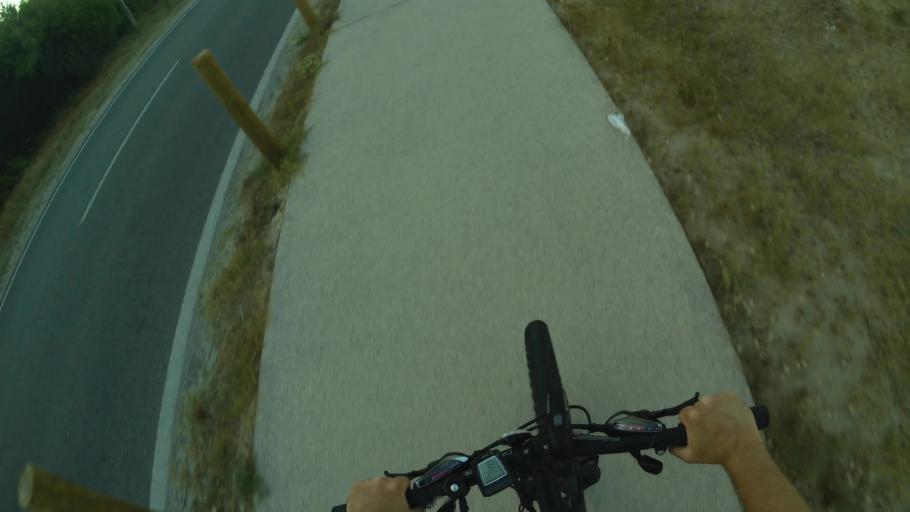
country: PT
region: Aveiro
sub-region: Ilhavo
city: Gafanha da Encarnacao
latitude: 40.5959
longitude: -8.7511
